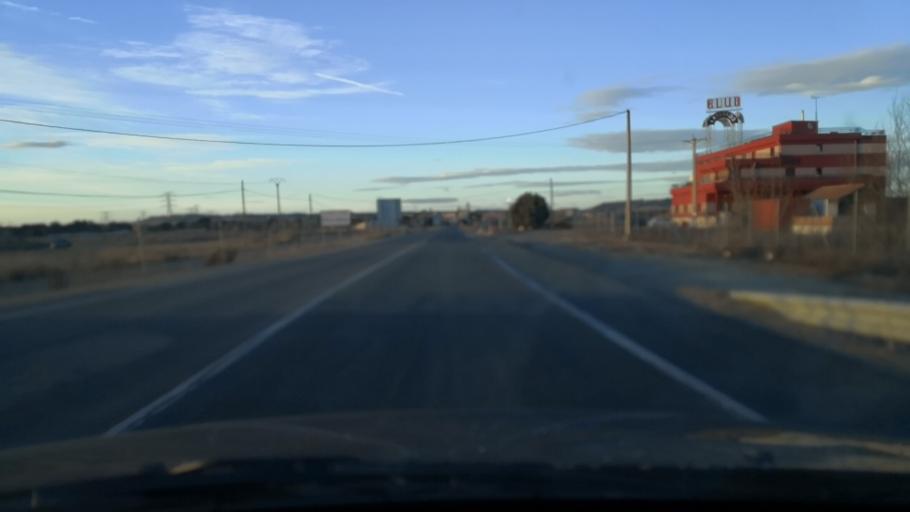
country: ES
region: Castille and Leon
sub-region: Provincia de Valladolid
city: Tordesillas
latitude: 41.4820
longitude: -4.9933
